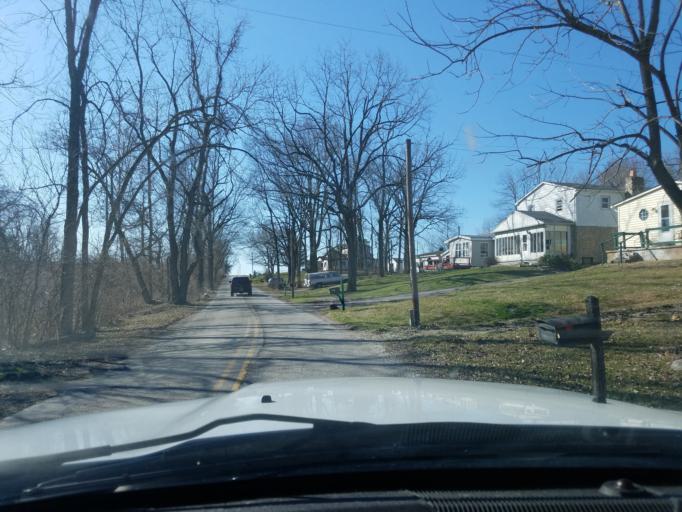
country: US
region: Indiana
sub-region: Johnson County
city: Franklin
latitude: 39.4954
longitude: -85.9657
